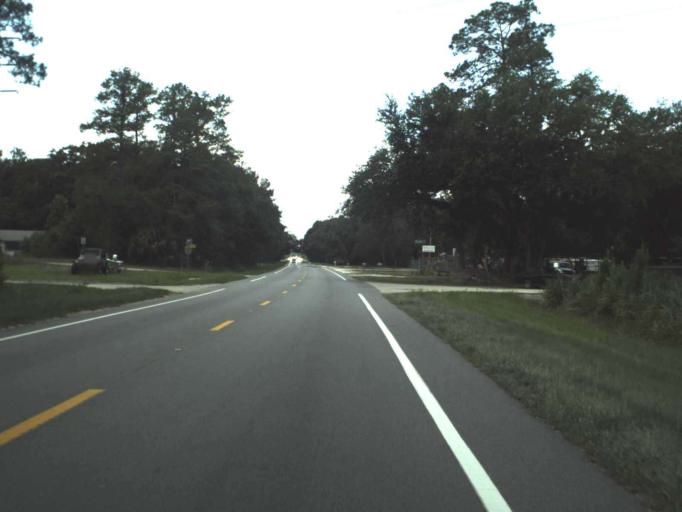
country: US
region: Florida
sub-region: Volusia County
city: West DeLand
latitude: 29.0167
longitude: -81.3730
